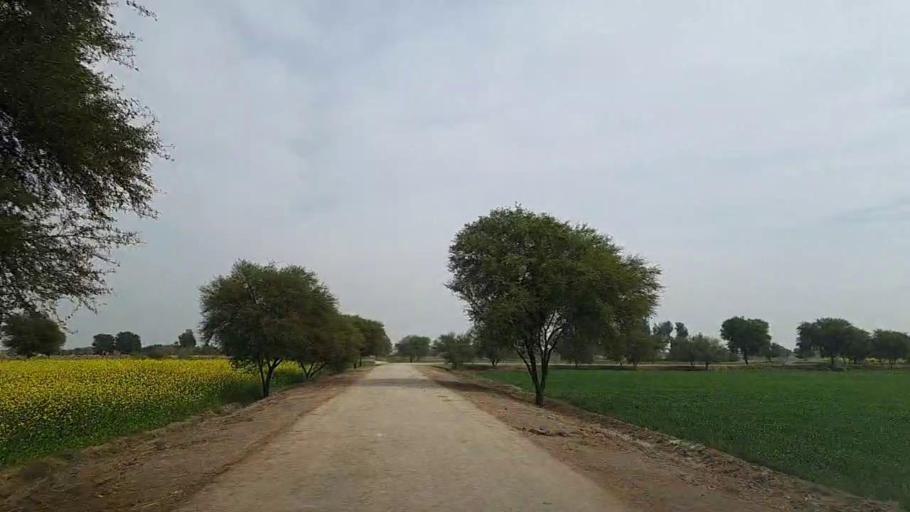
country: PK
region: Sindh
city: Daur
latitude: 26.4106
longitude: 68.4525
